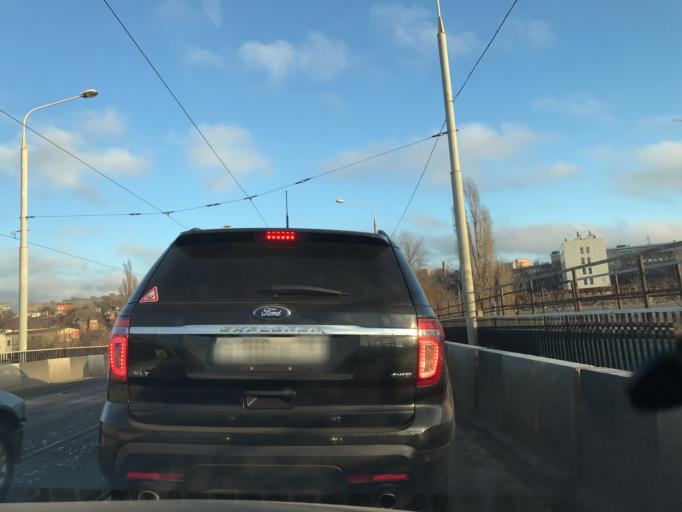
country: RU
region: Rostov
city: Rostov-na-Donu
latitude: 47.2229
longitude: 39.6855
